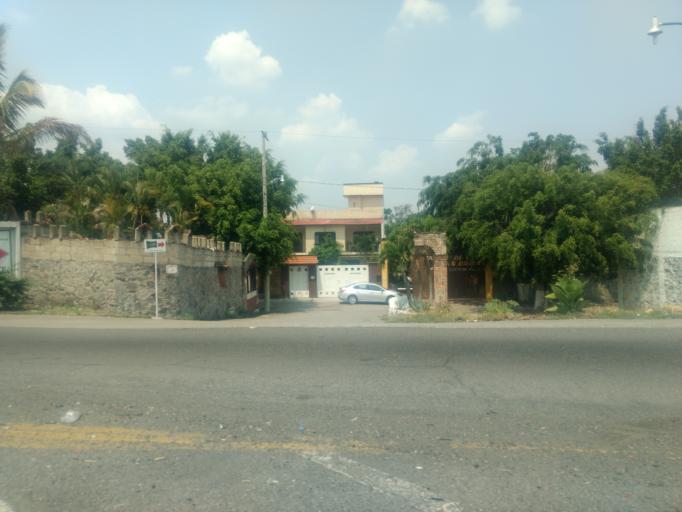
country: MX
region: Morelos
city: Temixco
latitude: 18.8485
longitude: -99.2196
